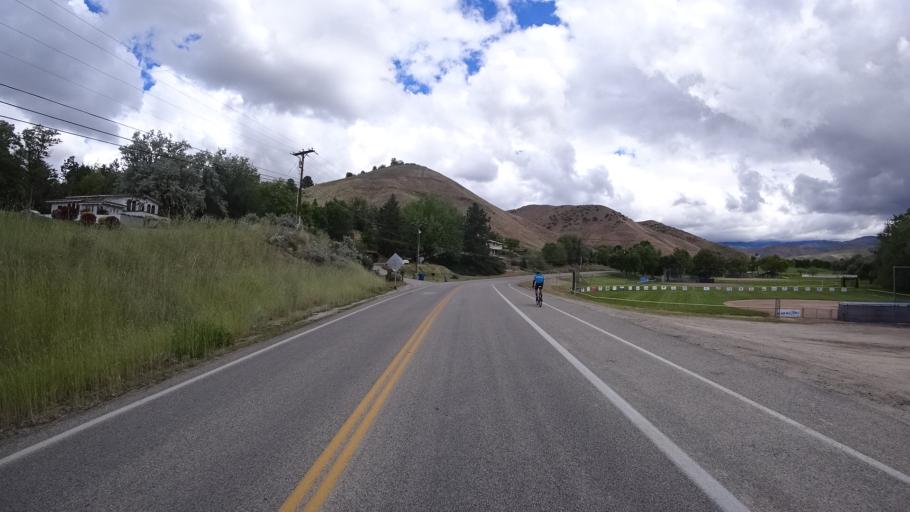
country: US
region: Idaho
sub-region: Ada County
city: Garden City
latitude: 43.6573
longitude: -116.2331
